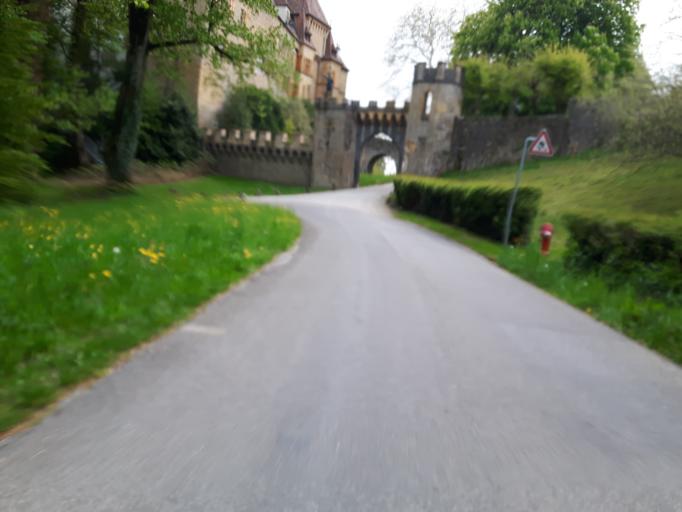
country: CH
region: Neuchatel
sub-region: Boudry District
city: Gorgier
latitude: 46.9090
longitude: 6.7858
